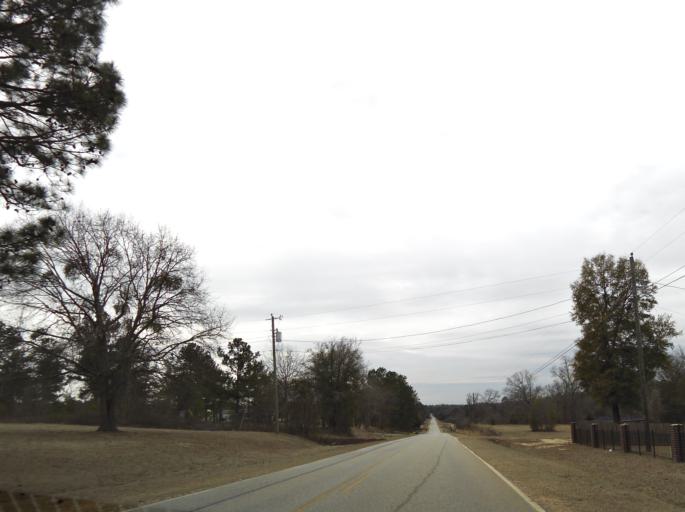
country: US
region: Georgia
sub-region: Peach County
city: Byron
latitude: 32.6181
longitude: -83.7854
